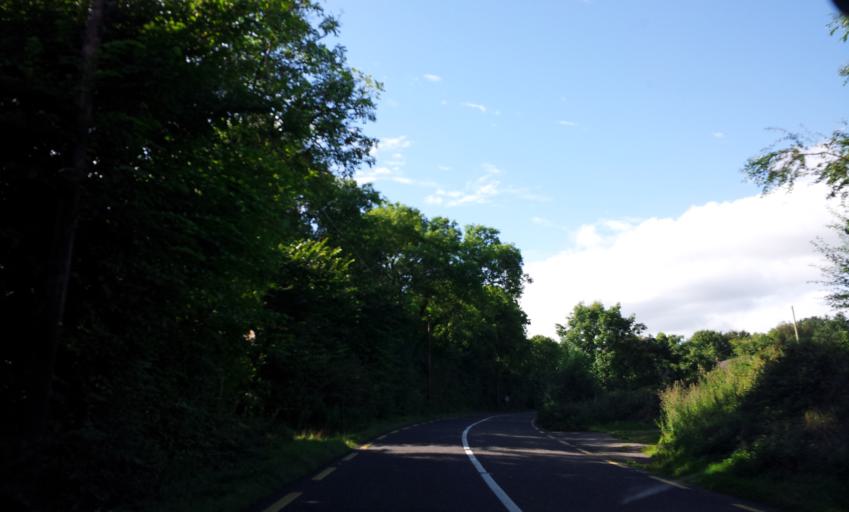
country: IE
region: Munster
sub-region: County Cork
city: Millstreet
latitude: 51.9472
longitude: -9.1774
